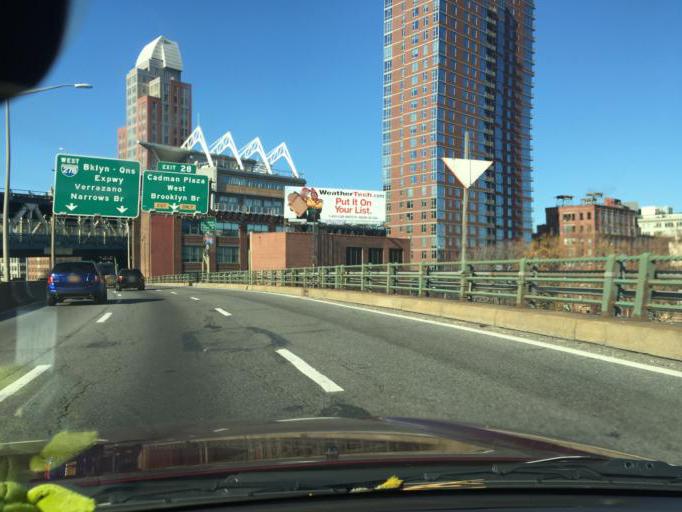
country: US
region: New York
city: New York City
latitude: 40.7009
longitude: -73.9859
